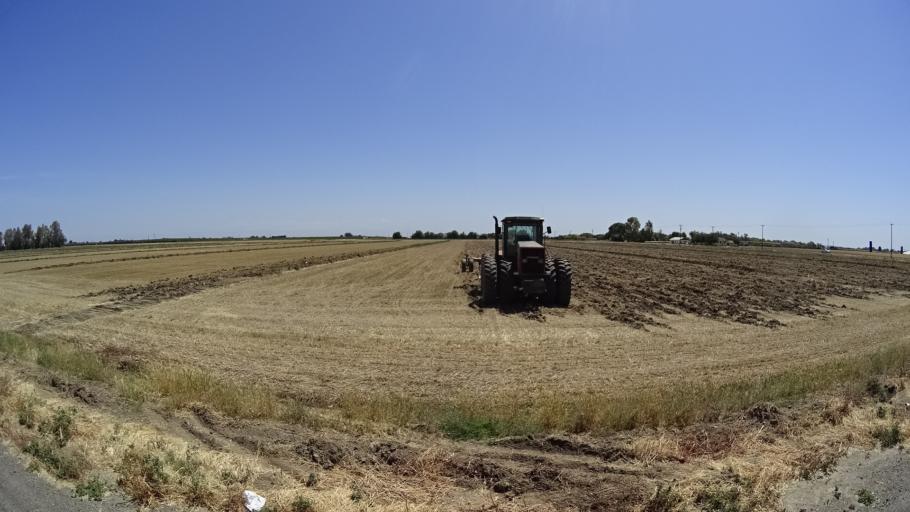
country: US
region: California
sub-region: Kings County
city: Lemoore
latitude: 36.2558
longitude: -119.7629
